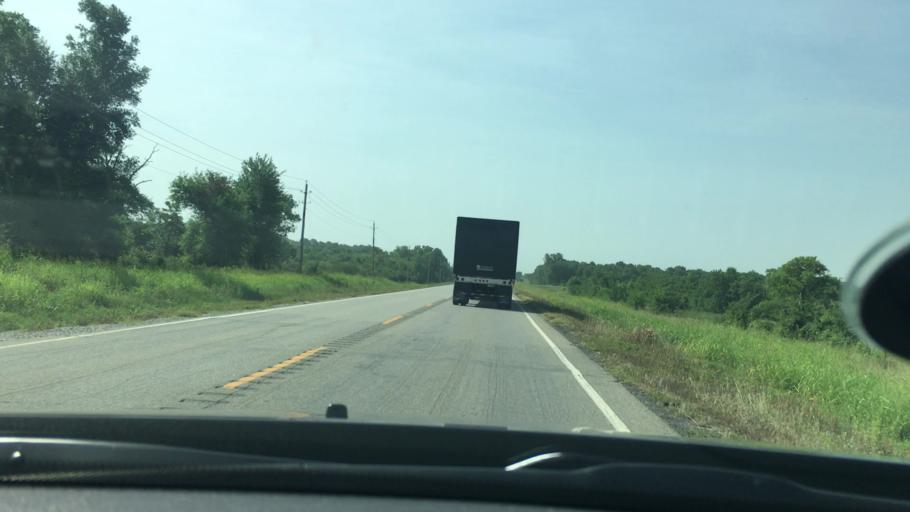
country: US
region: Oklahoma
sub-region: Coal County
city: Coalgate
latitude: 34.4525
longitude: -96.2108
